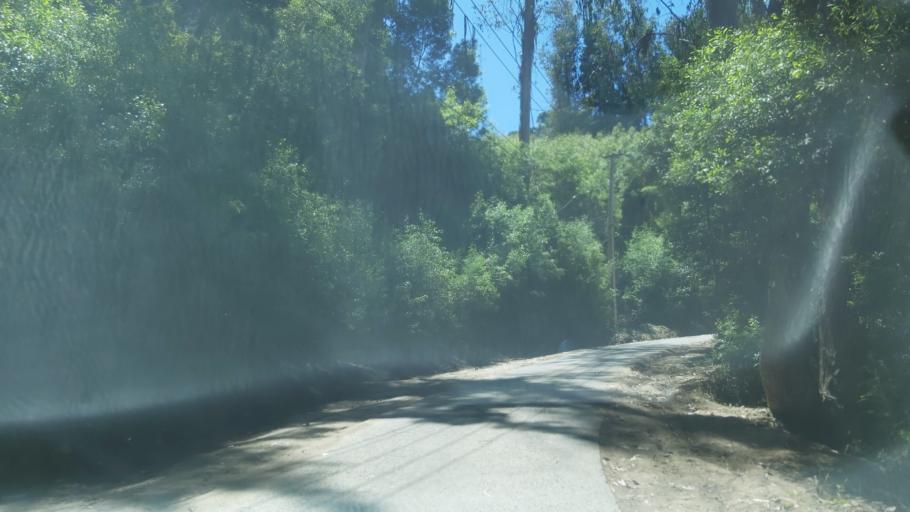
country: CL
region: Maule
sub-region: Provincia de Talca
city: Constitucion
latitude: -35.3239
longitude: -72.4133
